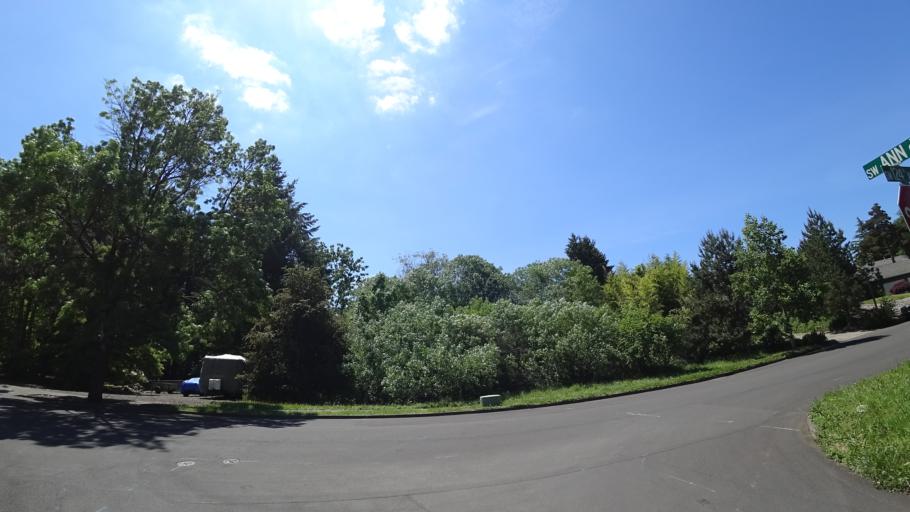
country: US
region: Oregon
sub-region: Washington County
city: King City
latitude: 45.4315
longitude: -122.8035
